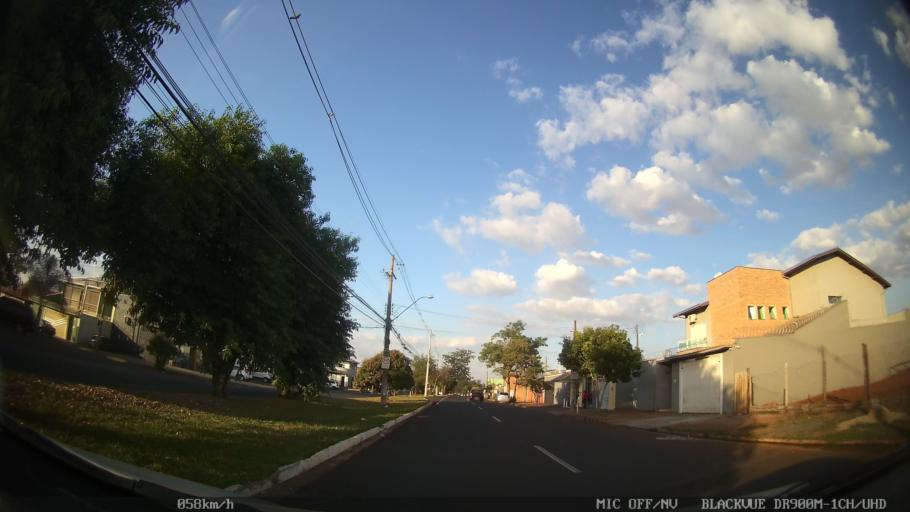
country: BR
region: Sao Paulo
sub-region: Ribeirao Preto
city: Ribeirao Preto
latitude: -21.1615
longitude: -47.7353
